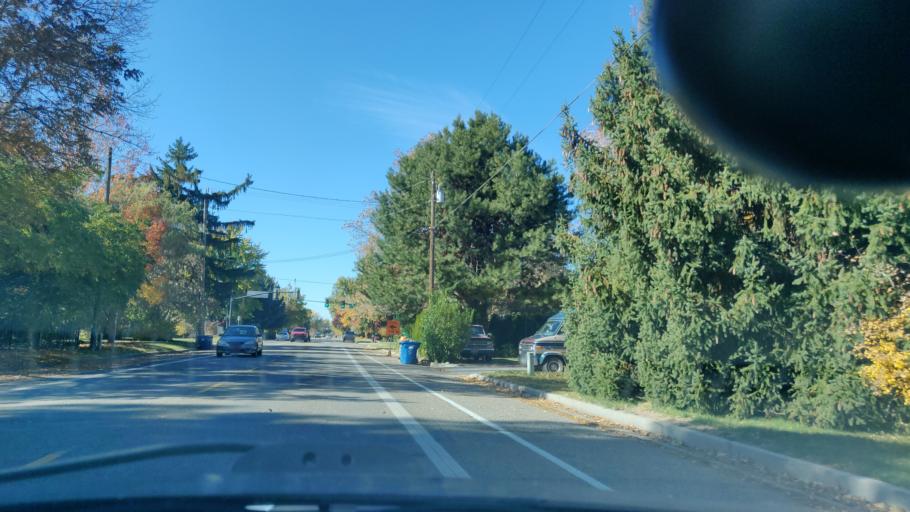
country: US
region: Idaho
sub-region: Ada County
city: Garden City
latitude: 43.5935
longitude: -116.2274
